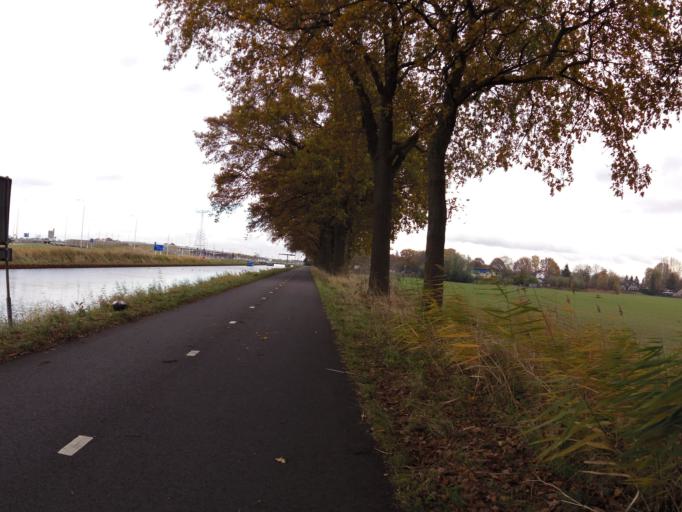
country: NL
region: North Brabant
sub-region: Gemeente Sint-Michielsgestel
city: Sint-Michielsgestel
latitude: 51.6814
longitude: 5.3630
